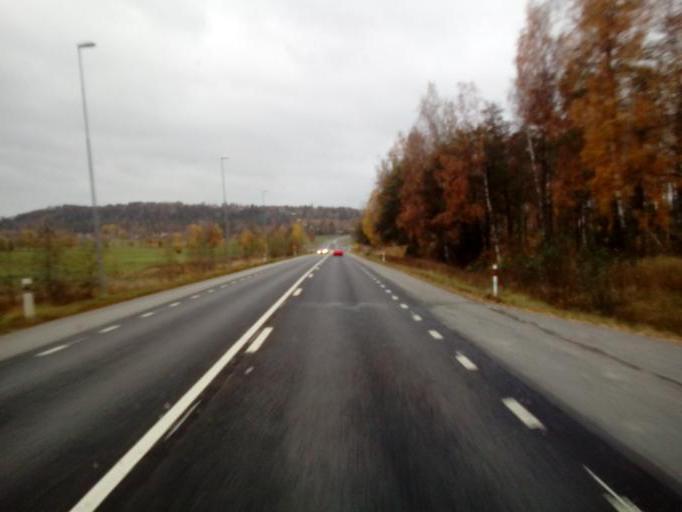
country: SE
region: OErebro
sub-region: Degerfors Kommun
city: Degerfors
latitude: 59.2590
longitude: 14.4411
